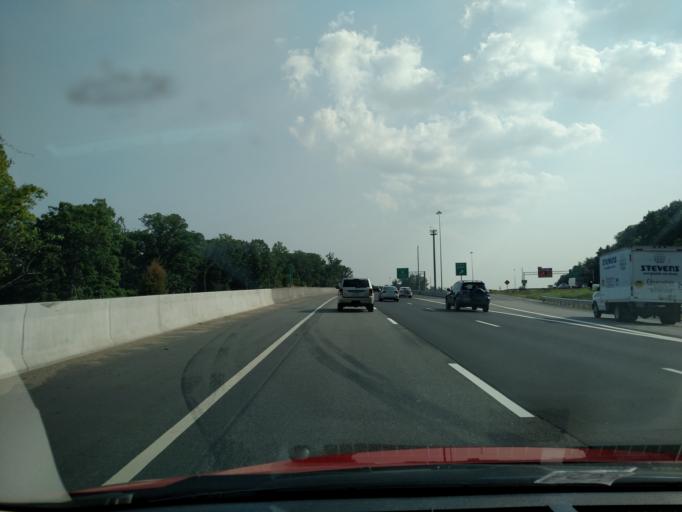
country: US
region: Virginia
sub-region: Fairfax County
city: Lorton
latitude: 38.6810
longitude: -77.2306
